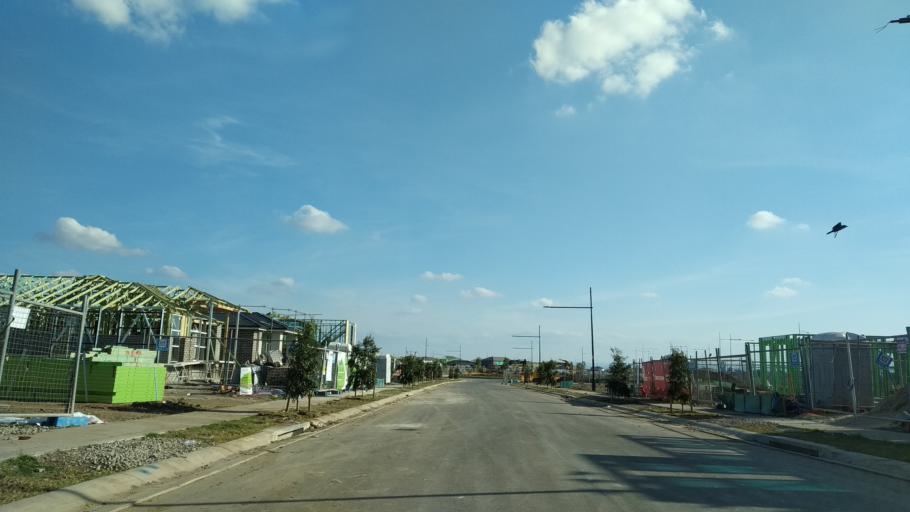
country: AU
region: New South Wales
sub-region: Blacktown
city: Hassall Grove
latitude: -33.6891
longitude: 150.8159
